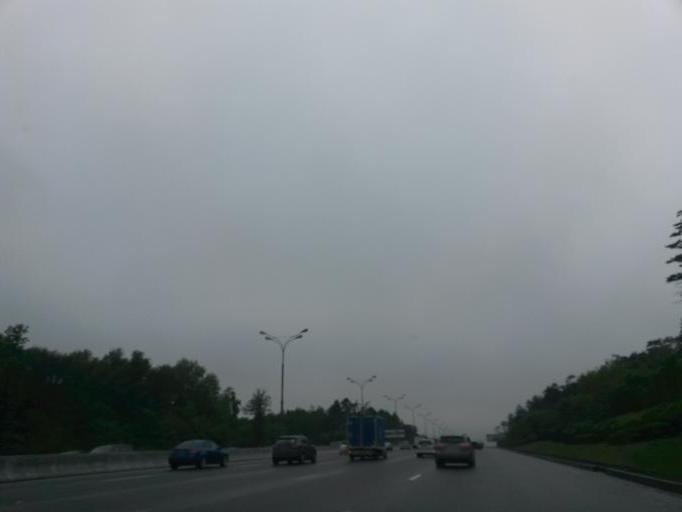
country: RU
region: Moscow
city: Chertanovo Yuzhnoye
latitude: 55.5844
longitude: 37.5597
